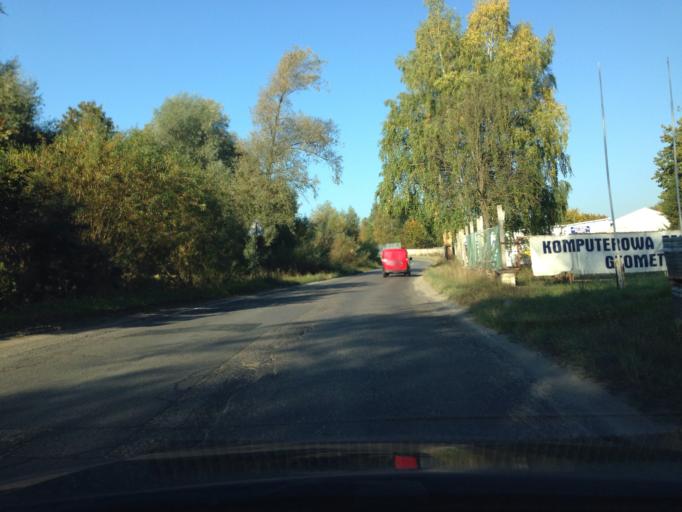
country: PL
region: Pomeranian Voivodeship
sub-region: Powiat gdanski
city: Rotmanka
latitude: 54.3100
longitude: 18.6191
